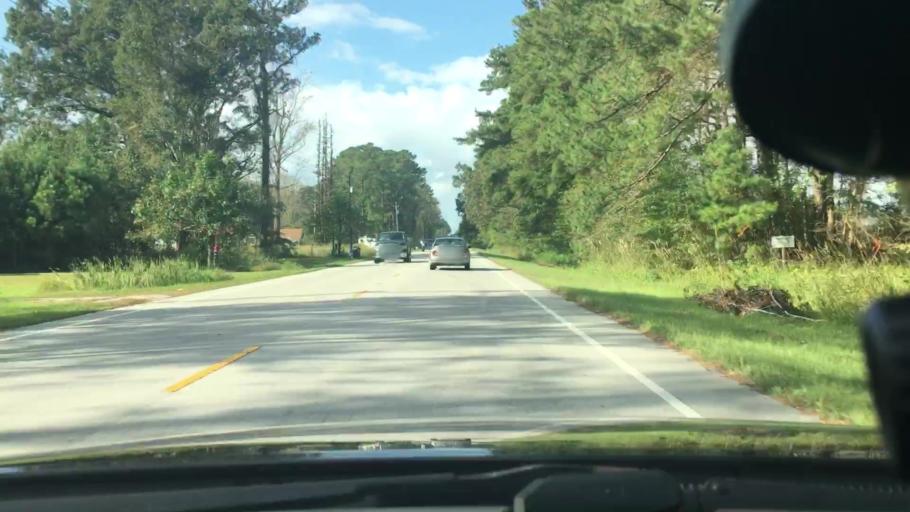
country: US
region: North Carolina
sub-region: Craven County
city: New Bern
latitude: 35.2045
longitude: -77.0585
